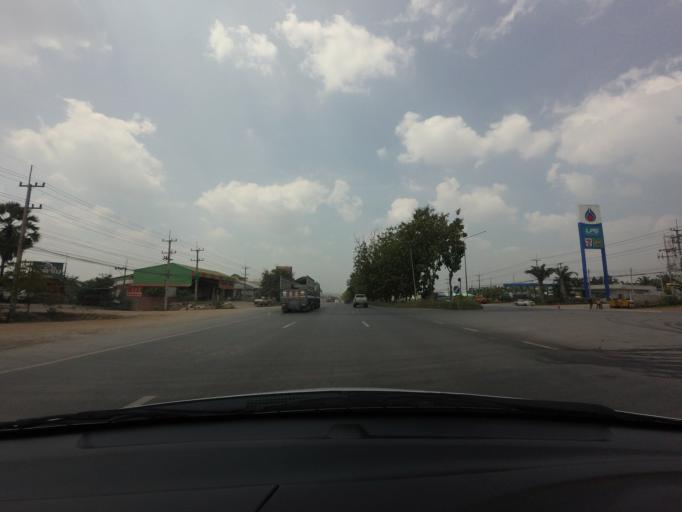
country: TH
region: Nakhon Ratchasima
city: Pak Chong
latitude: 14.6659
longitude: 101.4277
